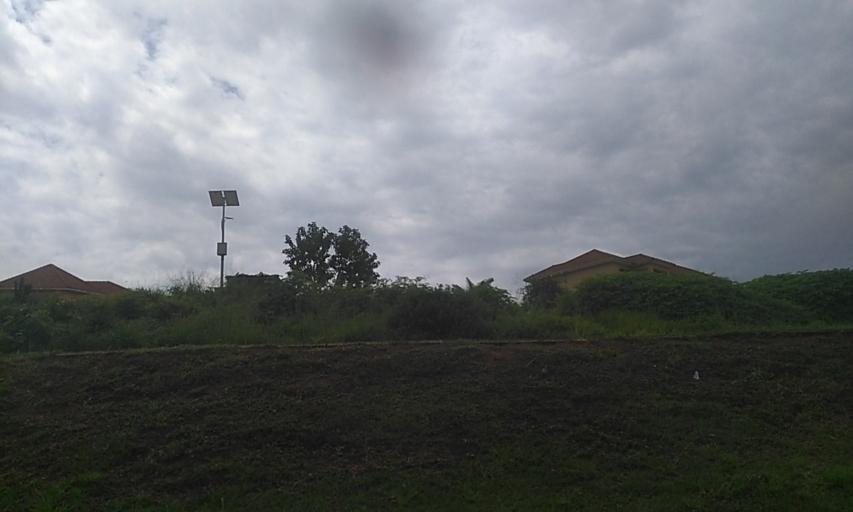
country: UG
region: Central Region
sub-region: Wakiso District
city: Kireka
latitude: 0.3621
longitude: 32.6343
